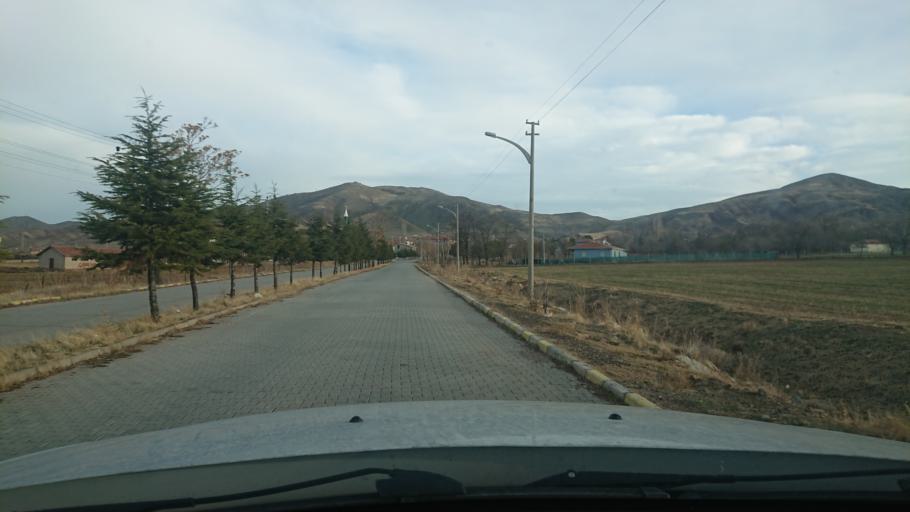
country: TR
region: Aksaray
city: Acipinar
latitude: 38.6105
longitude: 33.7781
